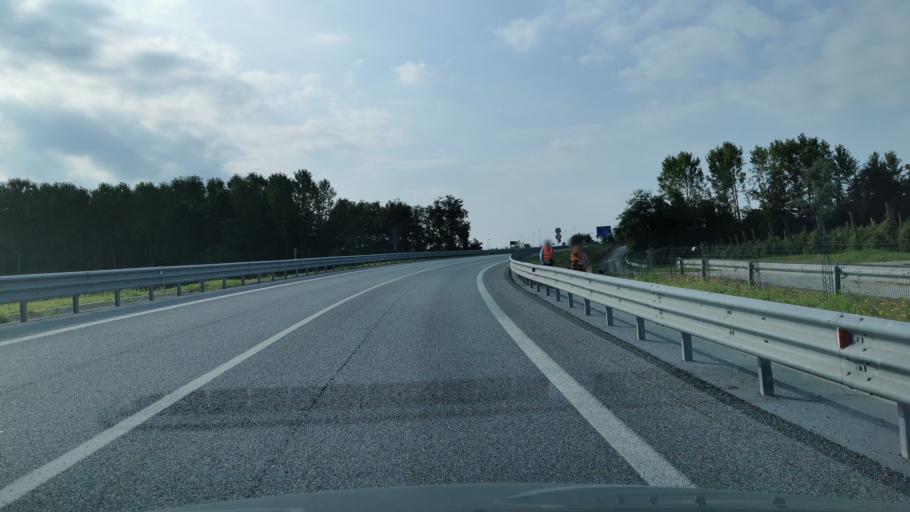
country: IT
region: Piedmont
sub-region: Provincia di Cuneo
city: Castelletto Stura
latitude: 44.4185
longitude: 7.5946
